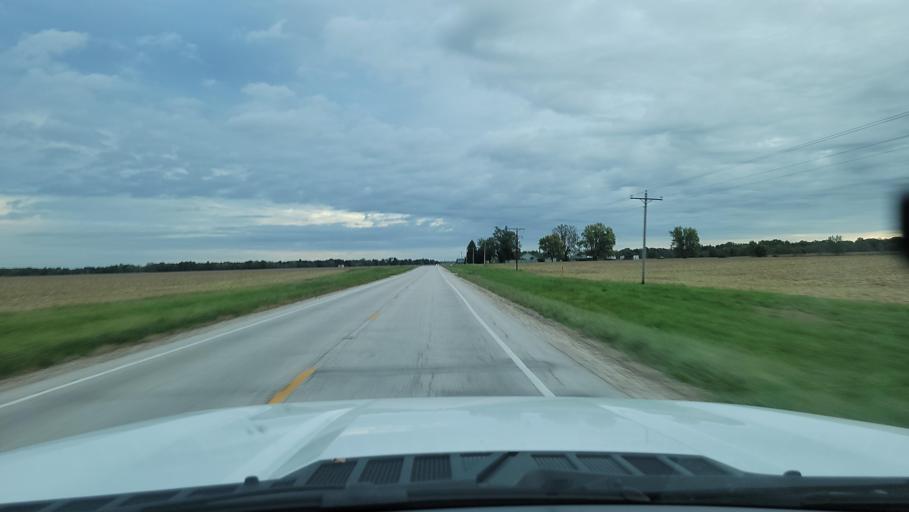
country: US
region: Illinois
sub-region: Schuyler County
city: Rushville
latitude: 40.0862
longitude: -90.6093
